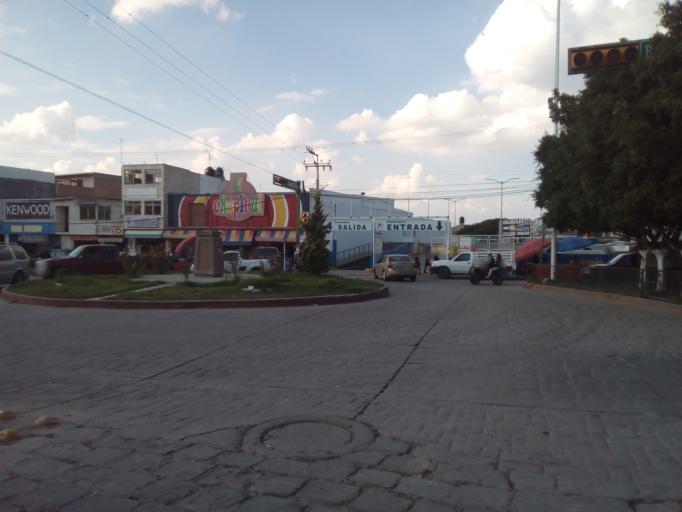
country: MX
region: Guerrero
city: San Luis de la Paz
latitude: 21.2965
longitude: -100.5243
